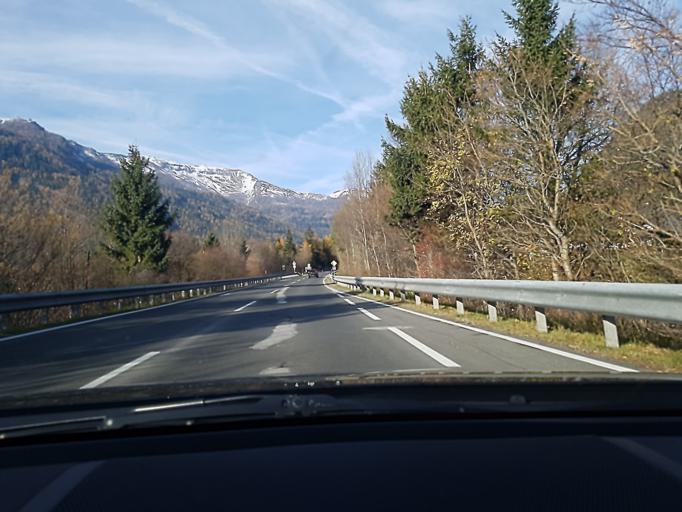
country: AT
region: Salzburg
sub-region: Politischer Bezirk Tamsweg
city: Mauterndorf
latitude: 47.1369
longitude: 13.6845
